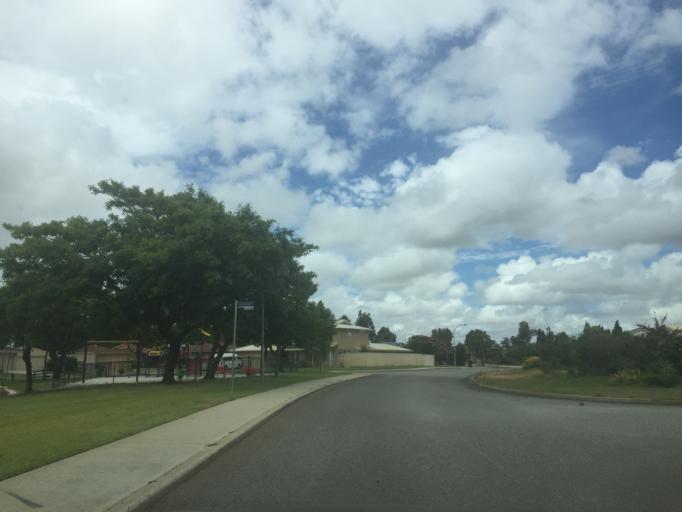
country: AU
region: Western Australia
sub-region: Gosnells
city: Thornlie
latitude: -32.0750
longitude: 115.9591
